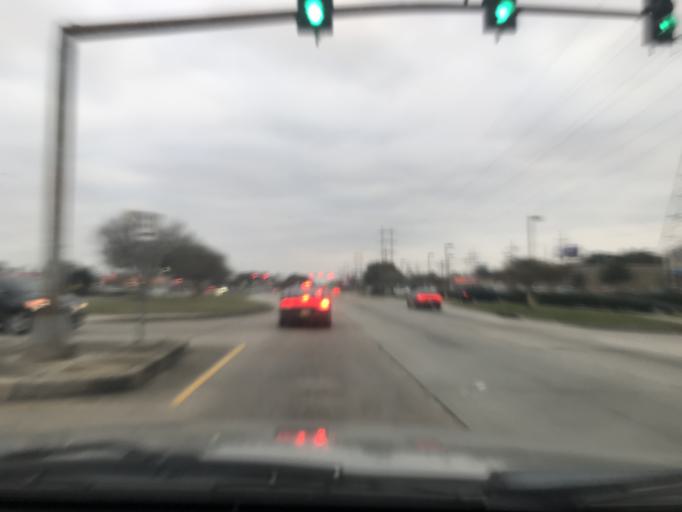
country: US
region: Louisiana
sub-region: Jefferson Parish
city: Woodmere
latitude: 29.8753
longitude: -90.0961
